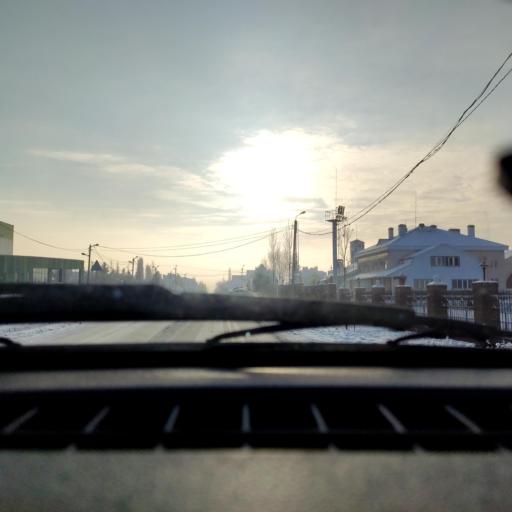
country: RU
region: Bashkortostan
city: Ufa
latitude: 54.6034
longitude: 55.9354
